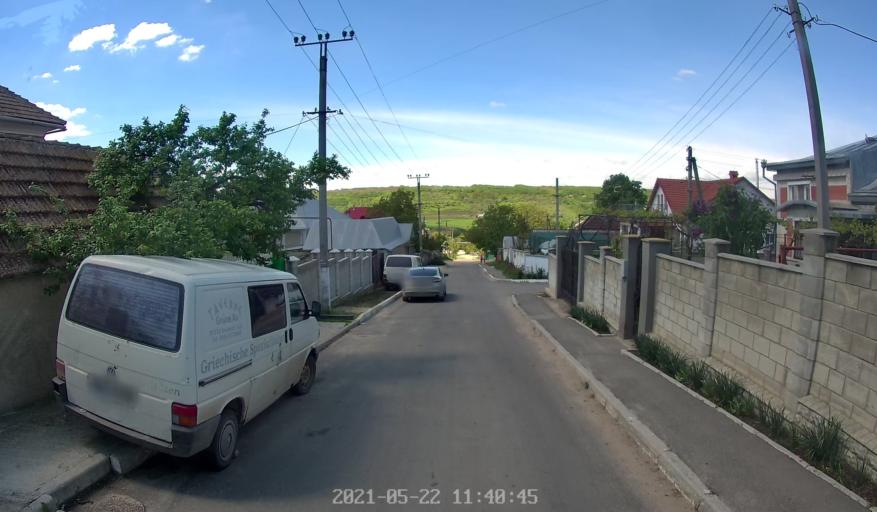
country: MD
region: Chisinau
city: Stauceni
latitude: 47.0986
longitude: 28.8309
